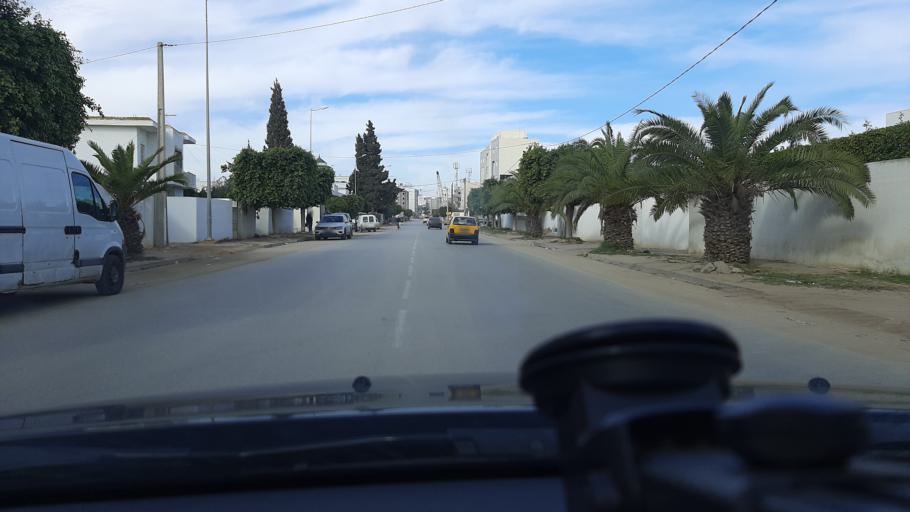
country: TN
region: Safaqis
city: Sfax
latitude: 34.7543
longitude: 10.7372
